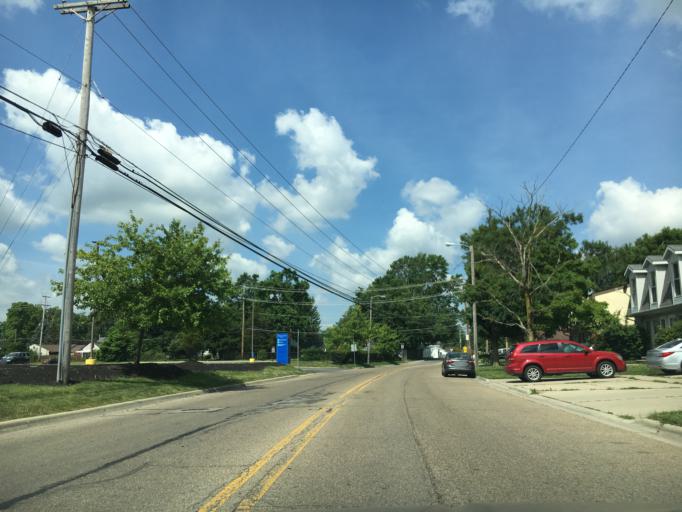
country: US
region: Ohio
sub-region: Franklin County
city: Lincoln Village
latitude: 39.9541
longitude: -83.1383
